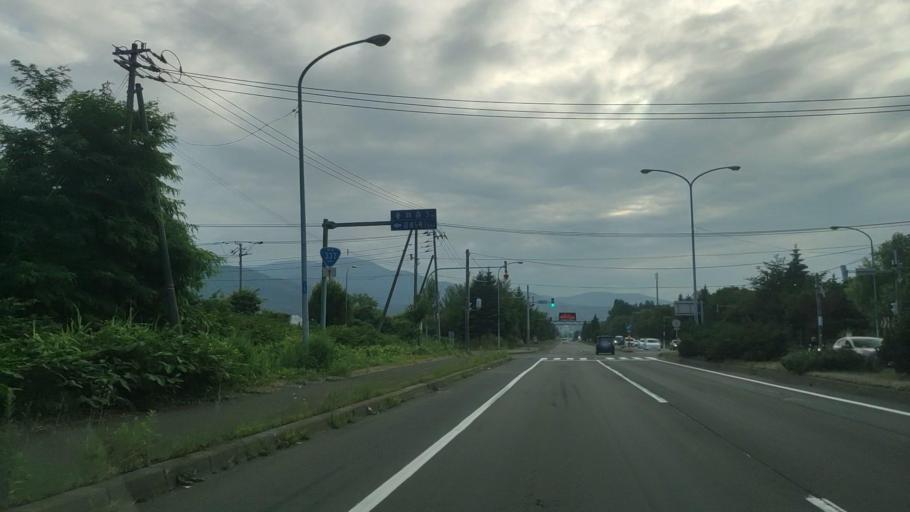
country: JP
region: Hokkaido
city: Sapporo
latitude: 43.1446
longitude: 141.1973
